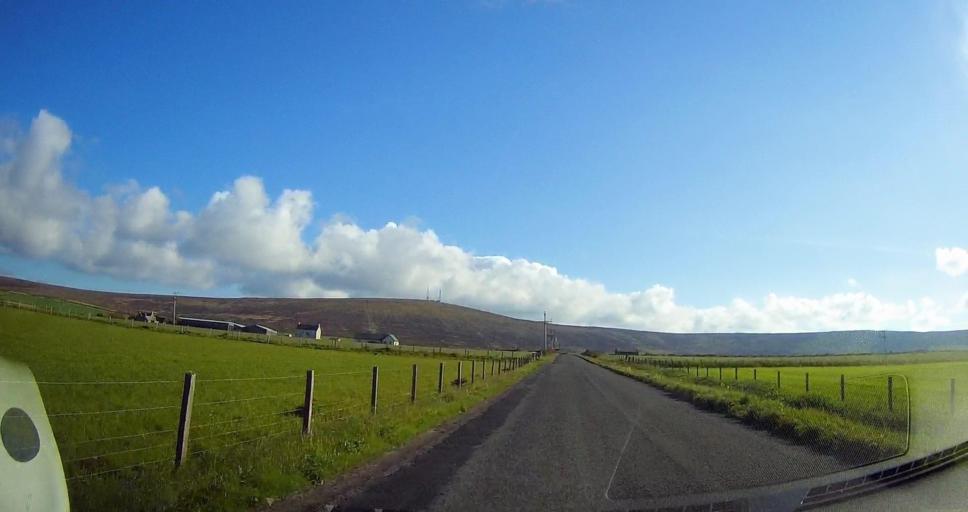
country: GB
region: Scotland
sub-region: Orkney Islands
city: Orkney
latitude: 58.9945
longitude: -3.0704
